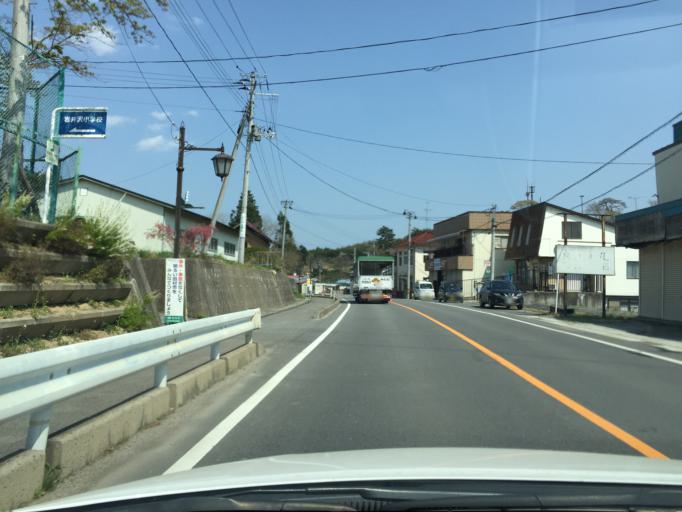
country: JP
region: Fukushima
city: Funehikimachi-funehiki
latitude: 37.4581
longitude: 140.7338
